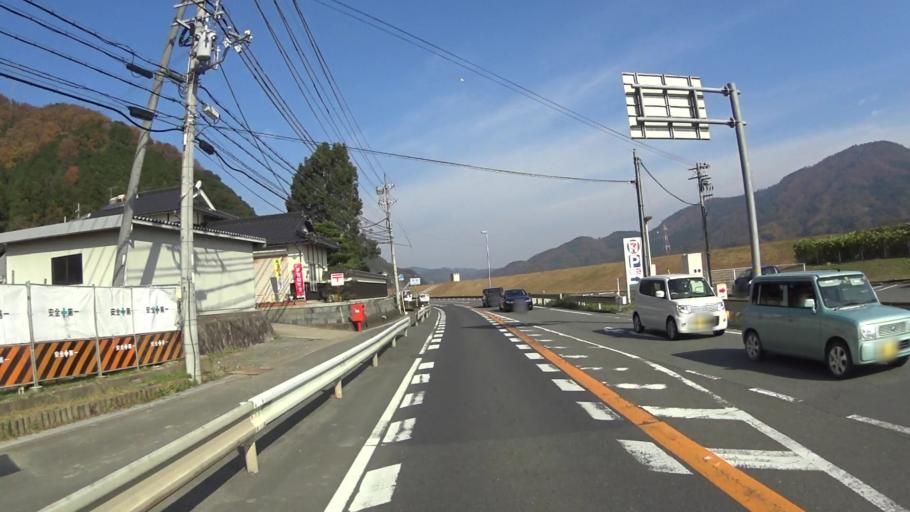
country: JP
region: Kyoto
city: Fukuchiyama
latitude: 35.3436
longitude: 135.1074
